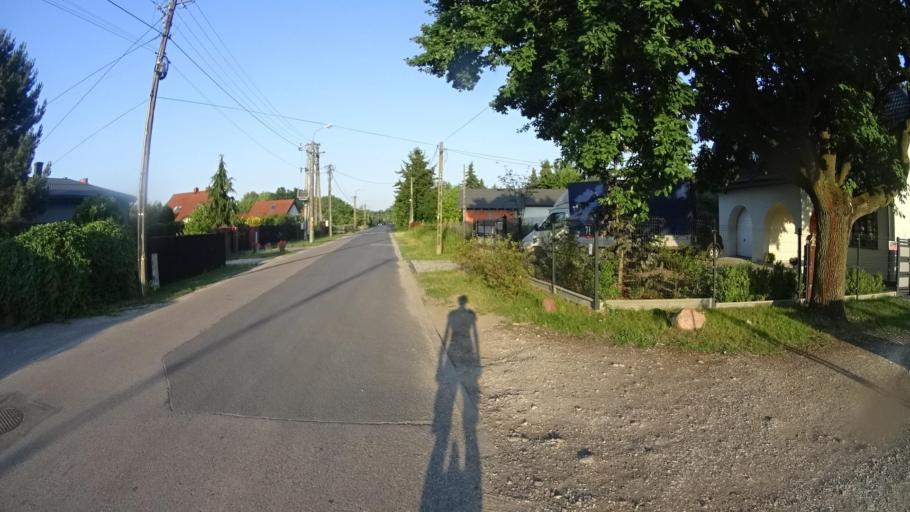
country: PL
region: Masovian Voivodeship
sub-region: Powiat warszawski zachodni
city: Stare Babice
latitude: 52.2657
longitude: 20.8457
